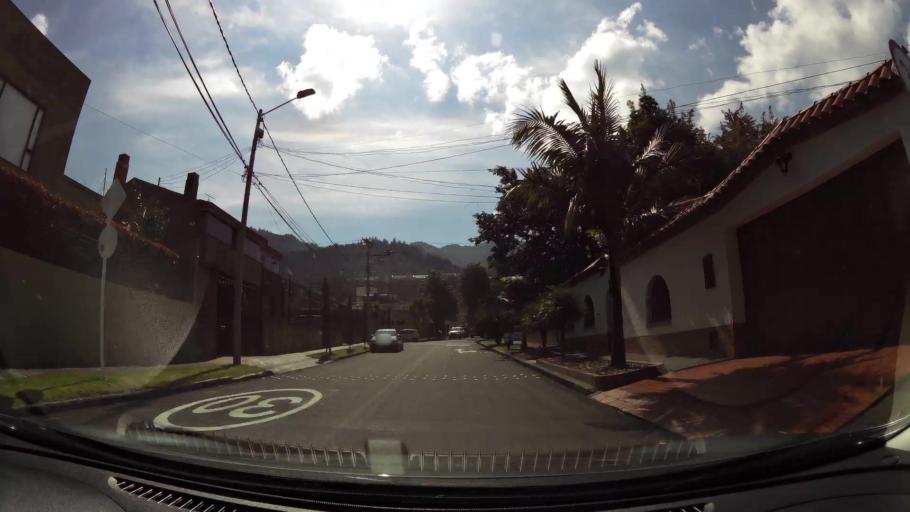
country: CO
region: Bogota D.C.
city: Barrio San Luis
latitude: 4.6906
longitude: -74.0315
